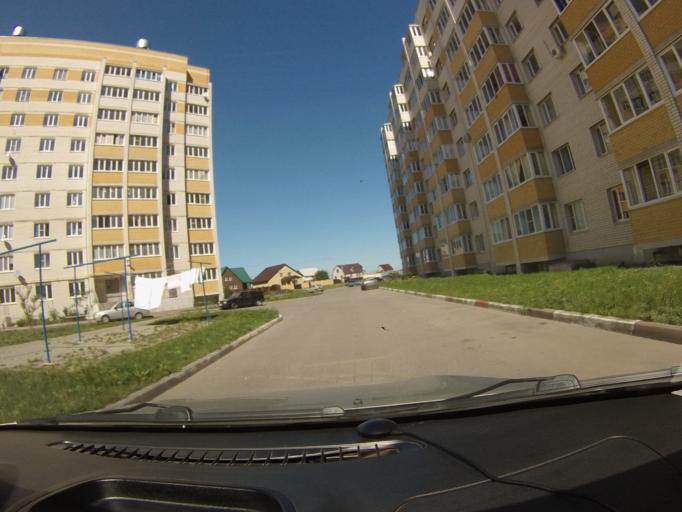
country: RU
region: Tambov
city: Tambov
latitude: 52.7766
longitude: 41.4014
